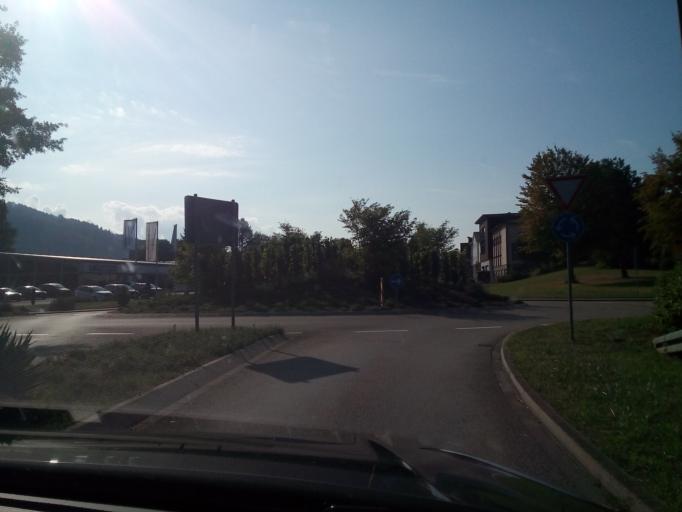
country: DE
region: Baden-Wuerttemberg
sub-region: Freiburg Region
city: Oberkirch
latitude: 48.5419
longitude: 8.0692
